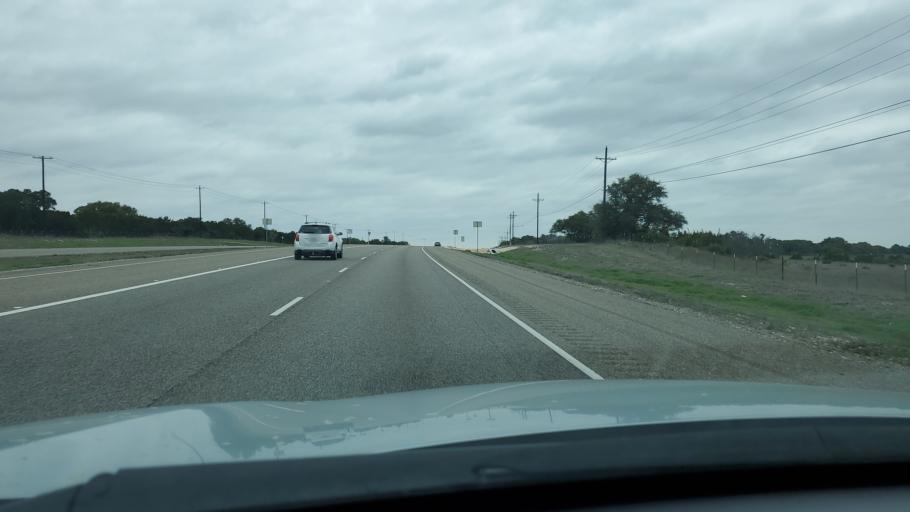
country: US
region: Texas
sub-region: Williamson County
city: Florence
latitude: 30.7922
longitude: -97.7662
